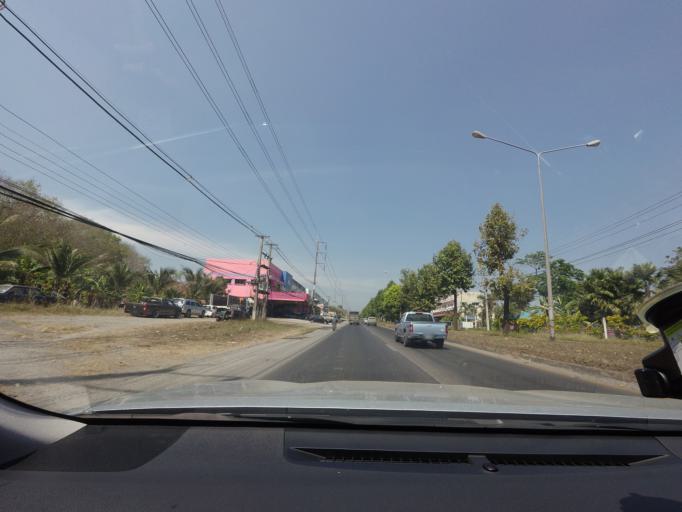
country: TH
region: Surat Thani
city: Kanchanadit
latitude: 9.1627
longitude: 99.4765
